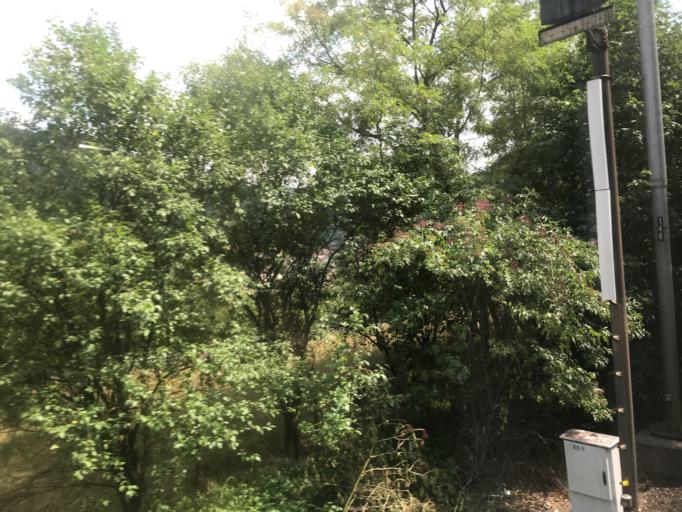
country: CZ
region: Ustecky
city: Povrly
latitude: 50.6989
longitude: 14.1979
